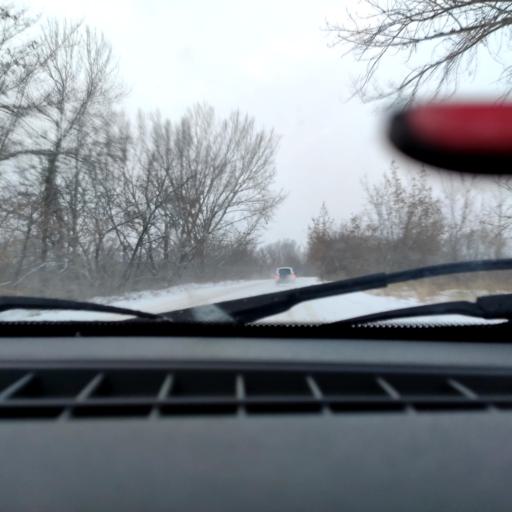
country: RU
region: Bashkortostan
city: Blagoveshchensk
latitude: 54.9075
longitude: 56.0085
